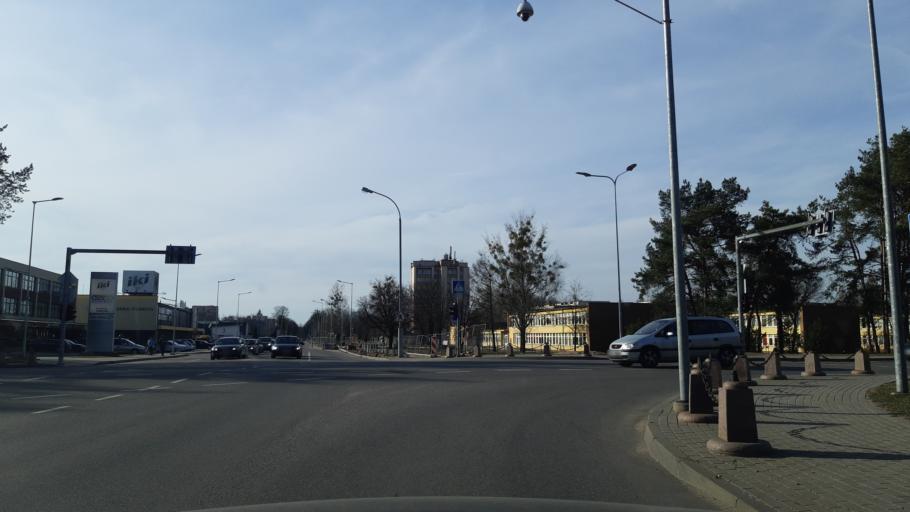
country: LT
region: Alytaus apskritis
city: Druskininkai
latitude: 54.0108
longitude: 23.9931
